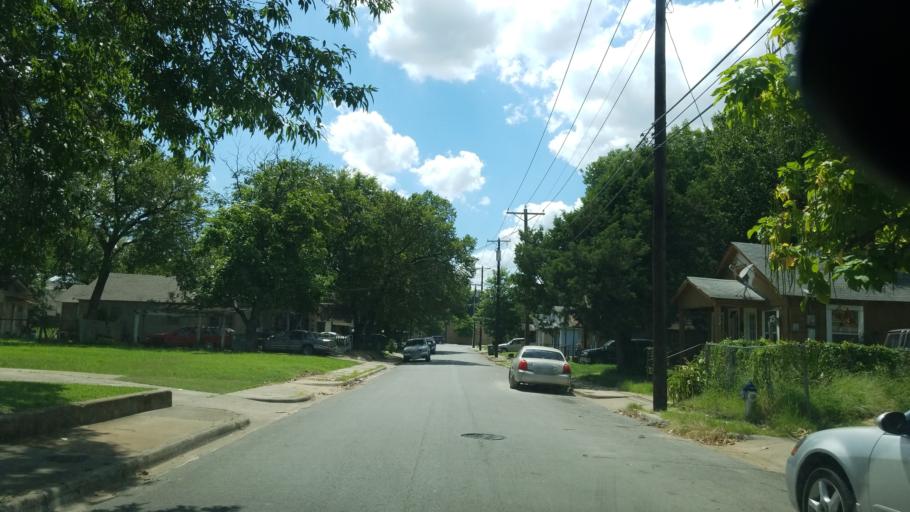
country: US
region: Texas
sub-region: Dallas County
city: Dallas
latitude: 32.7480
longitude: -96.7518
